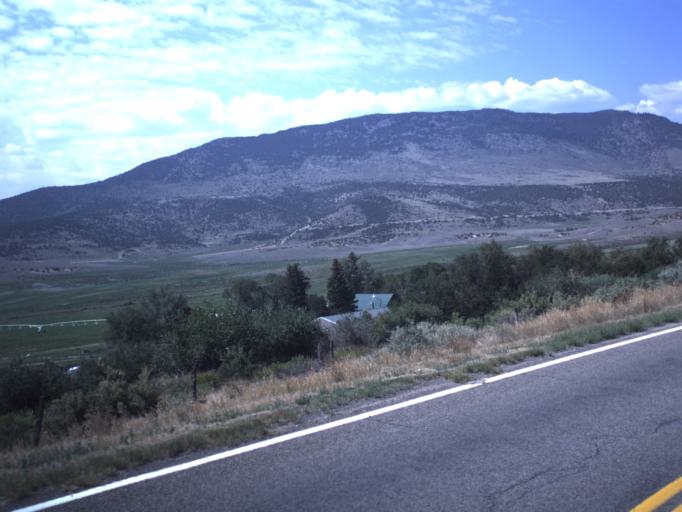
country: US
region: Utah
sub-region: Daggett County
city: Manila
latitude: 40.9754
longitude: -109.7664
